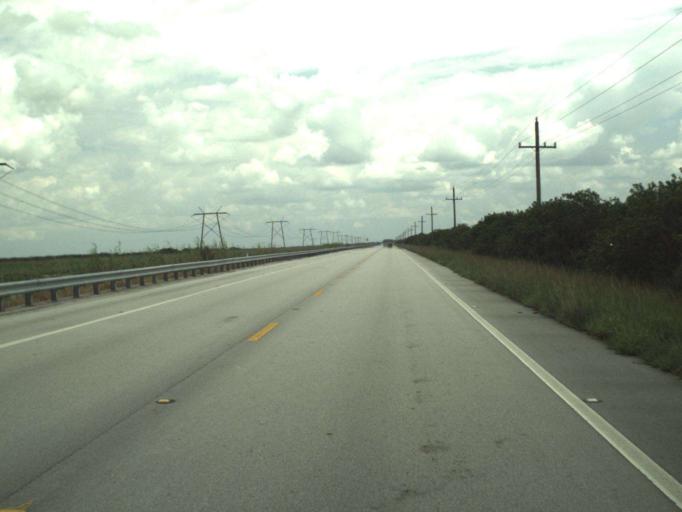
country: US
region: Florida
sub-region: Palm Beach County
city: Loxahatchee Groves
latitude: 26.7379
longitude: -80.4644
